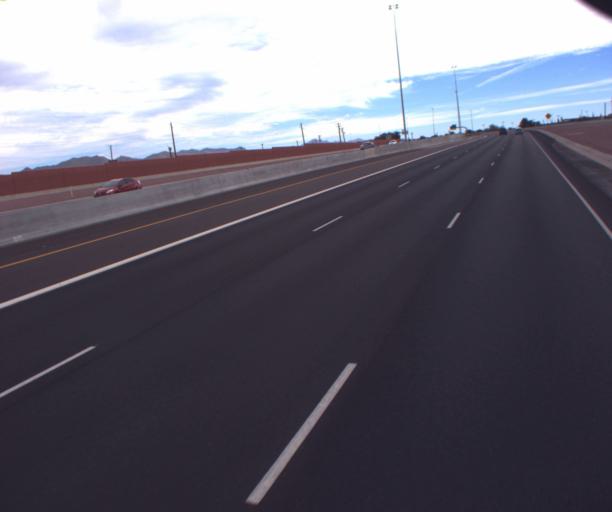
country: US
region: Arizona
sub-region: Maricopa County
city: Mesa
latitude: 33.4818
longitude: -111.7515
